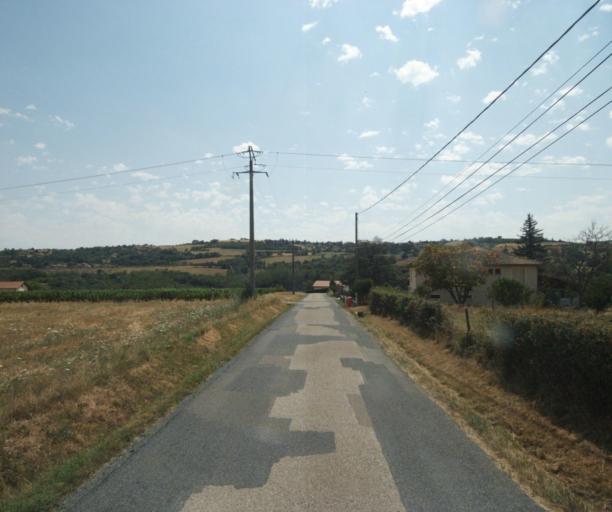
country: FR
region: Rhone-Alpes
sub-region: Departement du Rhone
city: Saint-Germain-Nuelles
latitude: 45.8435
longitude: 4.6286
